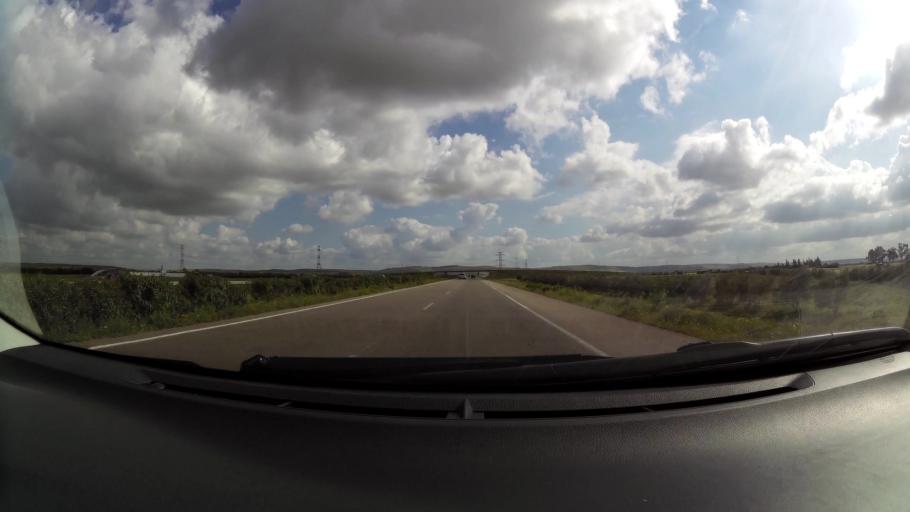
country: MA
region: Chaouia-Ouardigha
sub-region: Settat Province
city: Settat
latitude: 33.1169
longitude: -7.5810
